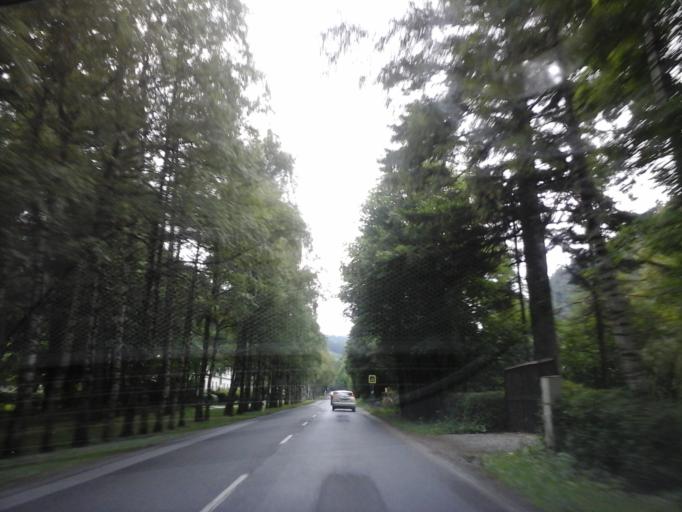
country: SK
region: Presovsky
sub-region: Okres Poprad
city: Zdiar
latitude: 49.2269
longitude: 20.3213
